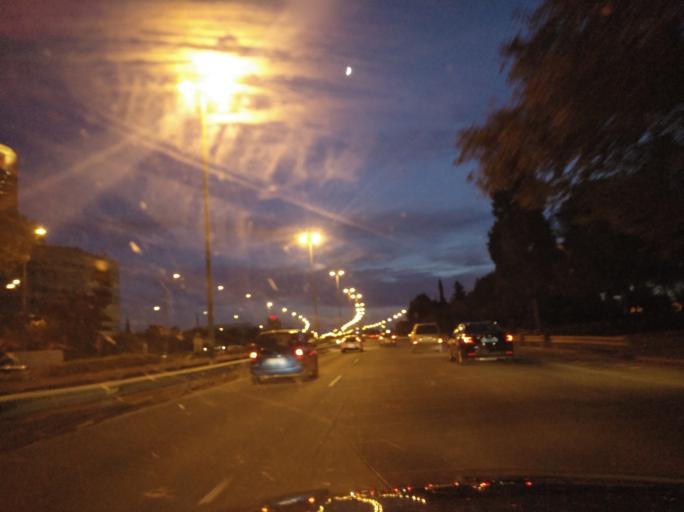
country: ES
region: Andalusia
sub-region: Provincia de Sevilla
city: Camas
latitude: 37.3953
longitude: -6.0128
